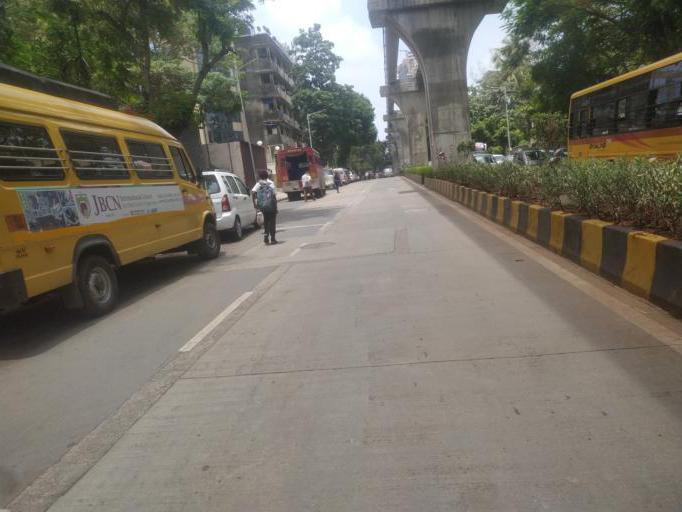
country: IN
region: Maharashtra
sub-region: Mumbai Suburban
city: Mumbai
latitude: 18.9947
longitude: 72.8402
